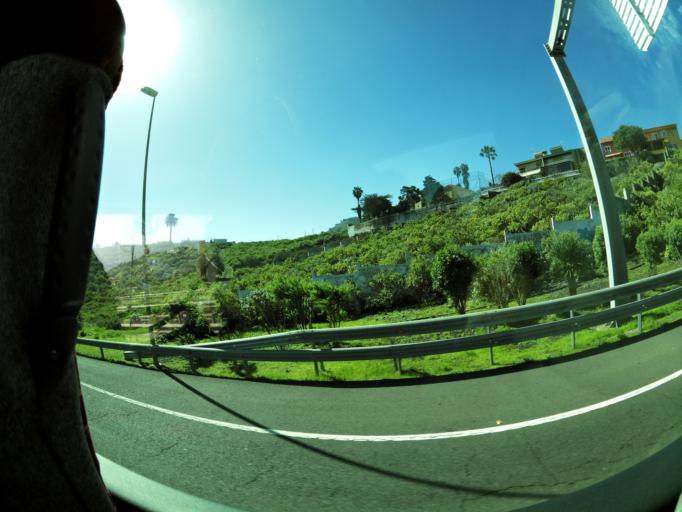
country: ES
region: Canary Islands
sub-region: Provincia de Las Palmas
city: Santa Brigida
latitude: 28.0500
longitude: -15.4558
